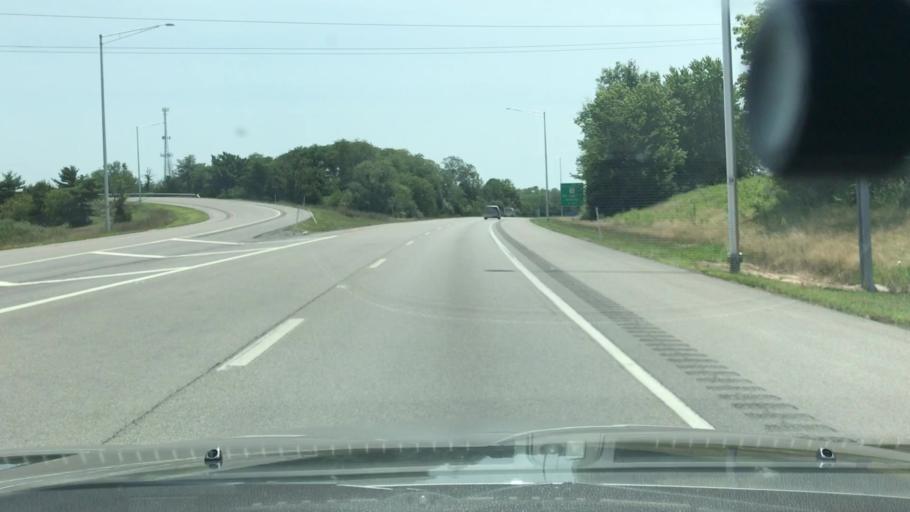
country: US
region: Illinois
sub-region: Jefferson County
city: Mount Vernon
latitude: 38.3373
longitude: -88.9597
